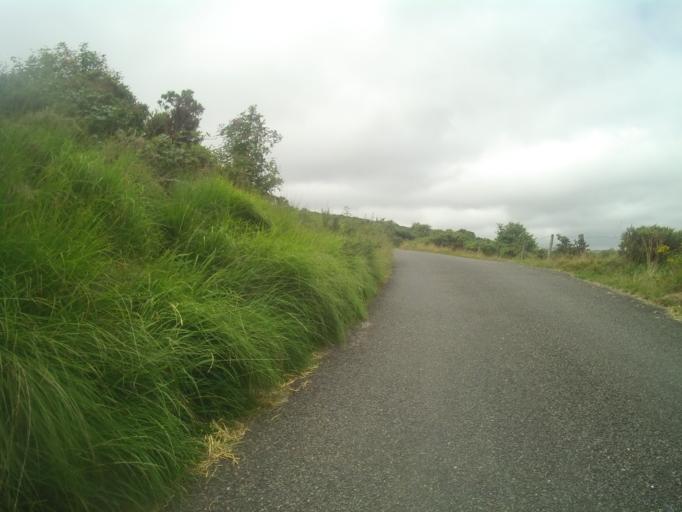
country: GB
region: England
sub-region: Devon
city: South Brent
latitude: 50.5322
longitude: -3.8894
